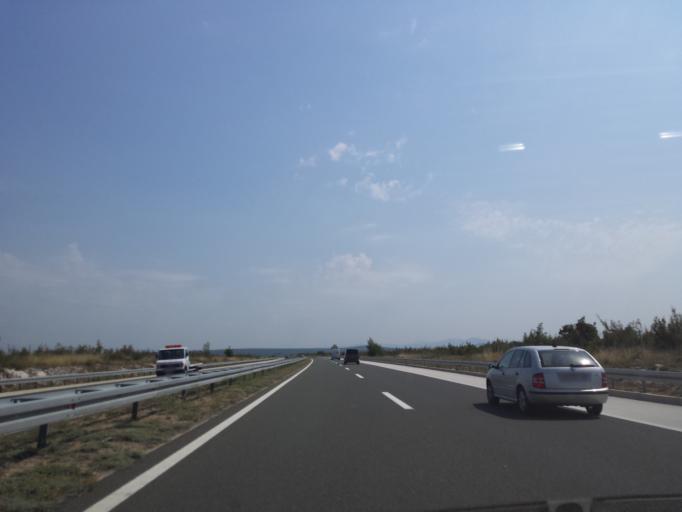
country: HR
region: Sibensko-Kniniska
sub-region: Grad Sibenik
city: Pirovac
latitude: 43.9061
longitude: 15.7611
